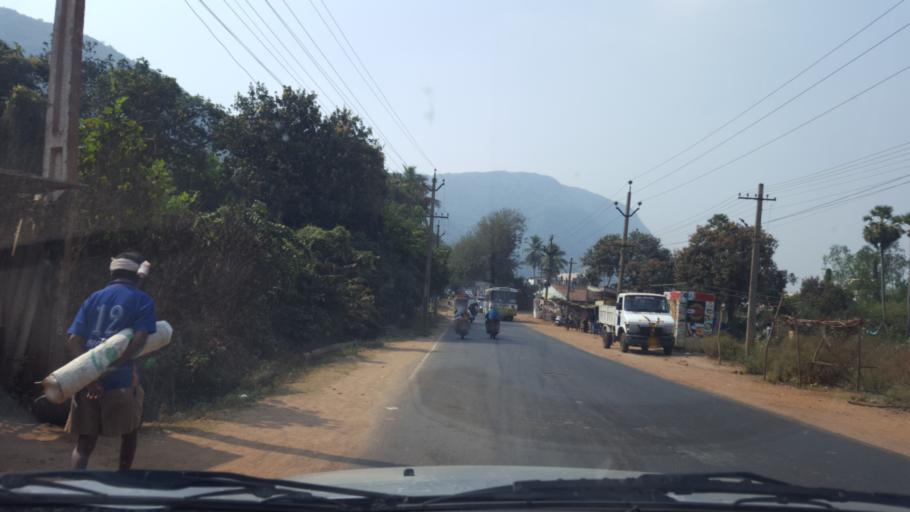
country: IN
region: Andhra Pradesh
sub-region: Vishakhapatnam
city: Vepagunta
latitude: 17.7770
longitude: 83.2504
